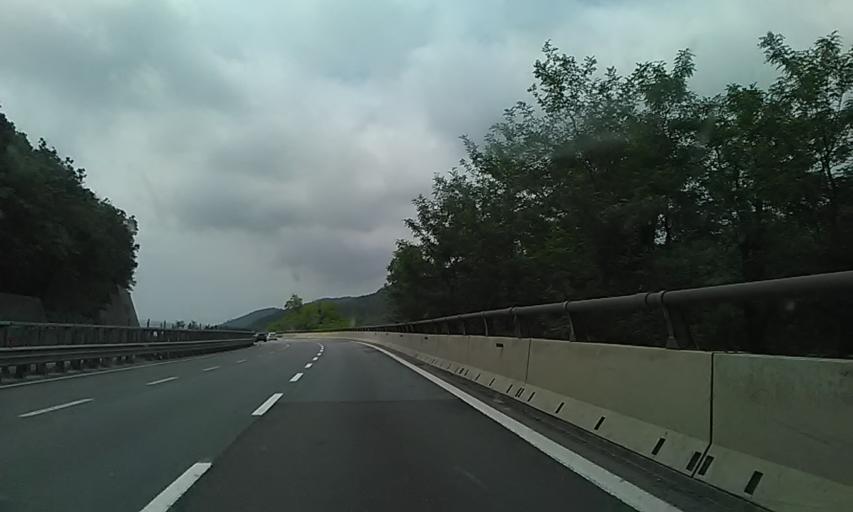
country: IT
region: Liguria
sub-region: Provincia di Genova
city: Masone
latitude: 44.4768
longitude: 8.7352
